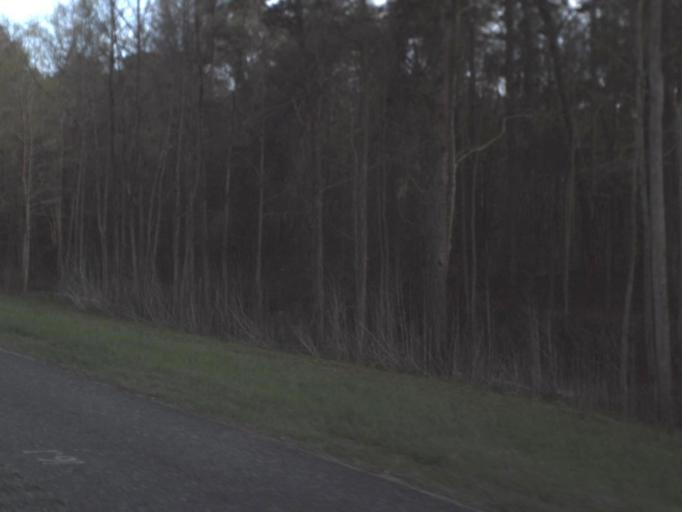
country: US
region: Florida
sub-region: Leon County
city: Tallahassee
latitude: 30.4782
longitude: -84.1423
